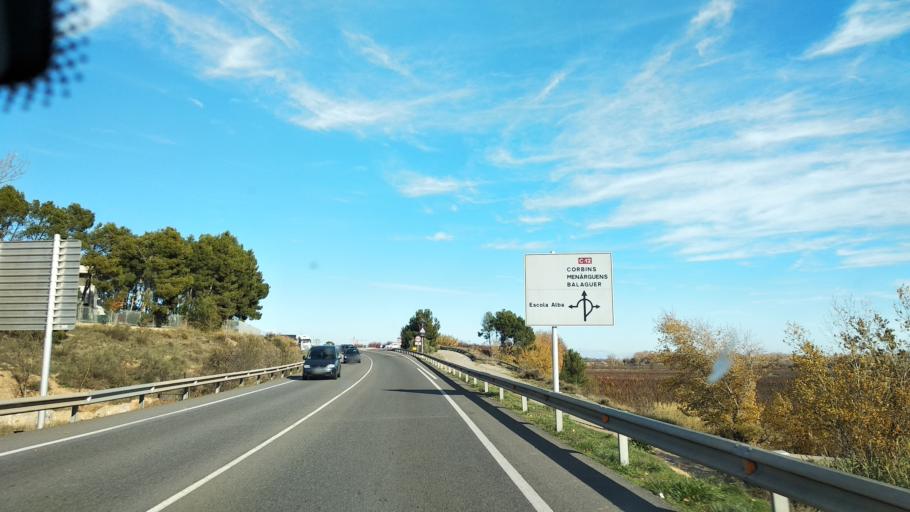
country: ES
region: Catalonia
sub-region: Provincia de Lleida
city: Alcoletge
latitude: 41.6588
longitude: 0.6606
